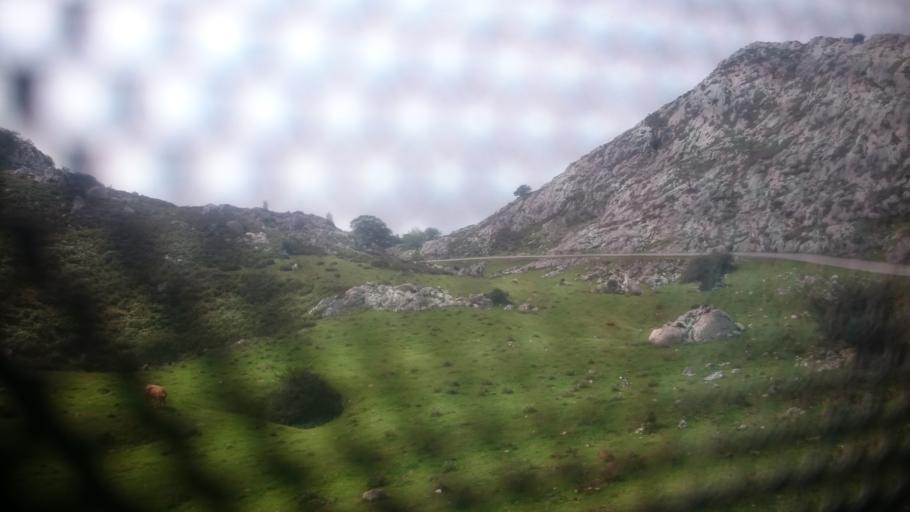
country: ES
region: Asturias
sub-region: Province of Asturias
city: Amieva
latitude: 43.2755
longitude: -4.9952
